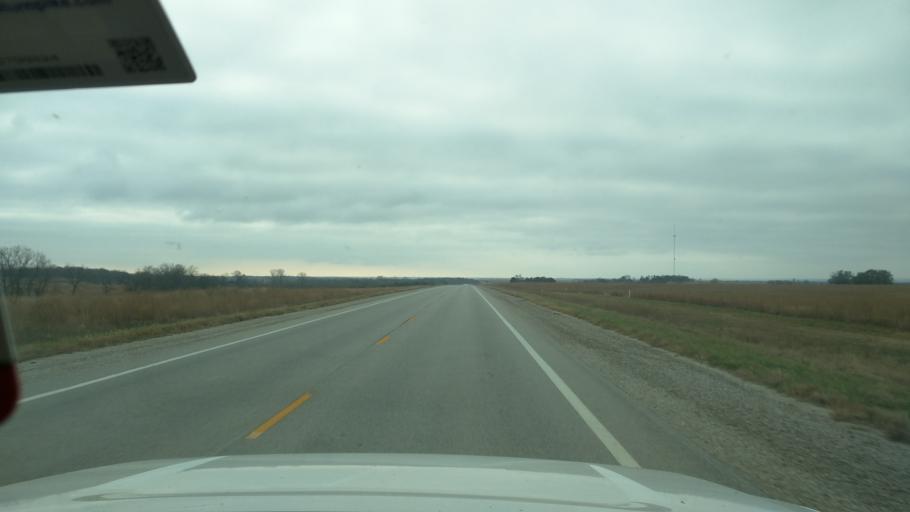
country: US
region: Kansas
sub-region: Elk County
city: Howard
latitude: 37.5592
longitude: -96.2532
